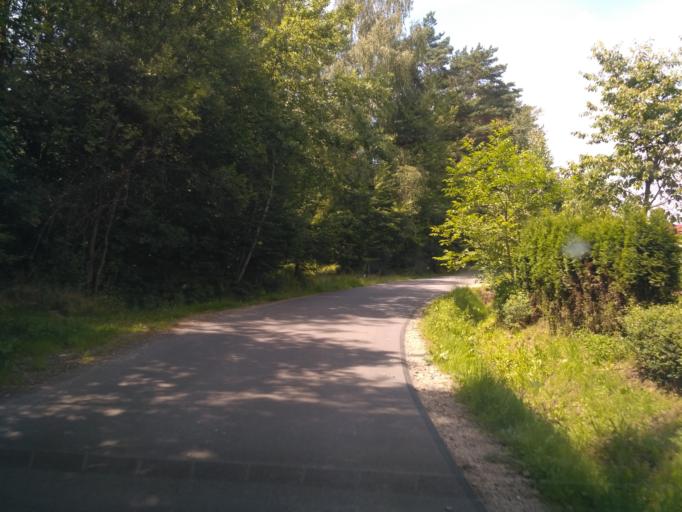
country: PL
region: Subcarpathian Voivodeship
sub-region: Powiat strzyzowski
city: Jawornik
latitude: 49.8551
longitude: 21.8941
